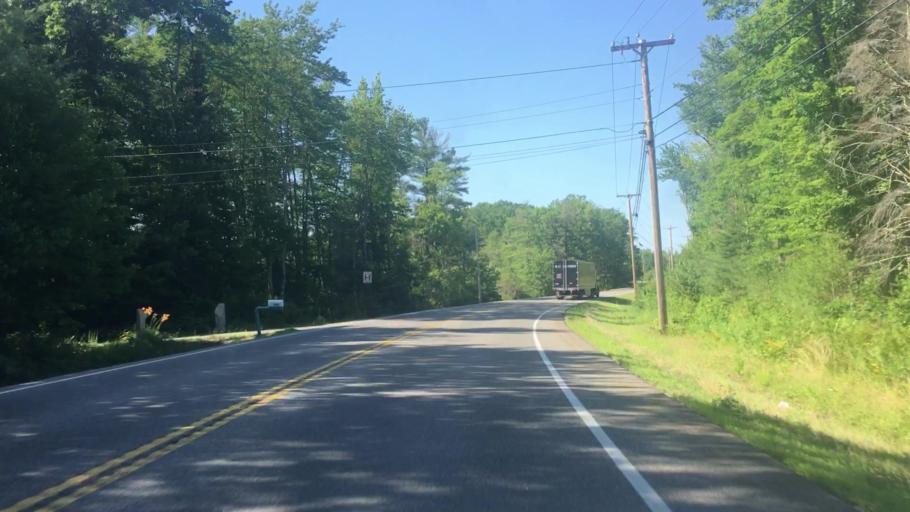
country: US
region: Maine
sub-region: York County
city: Dayton
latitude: 43.5590
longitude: -70.4987
